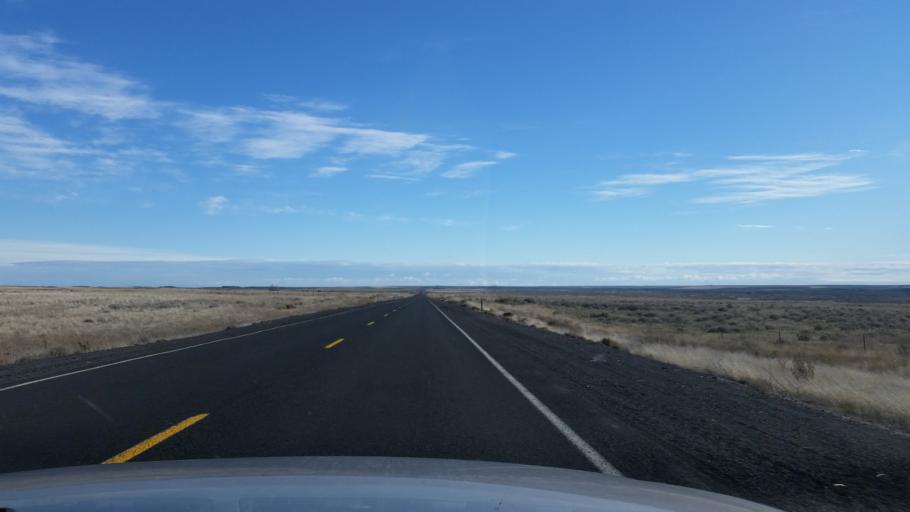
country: US
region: Washington
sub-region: Grant County
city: Warden
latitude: 47.3497
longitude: -118.9335
